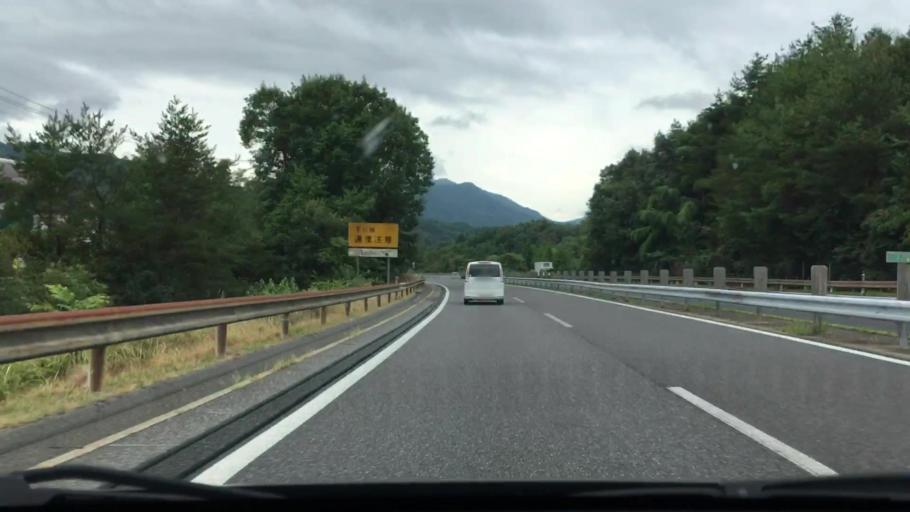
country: JP
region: Hiroshima
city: Hiroshima-shi
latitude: 34.6862
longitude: 132.5631
